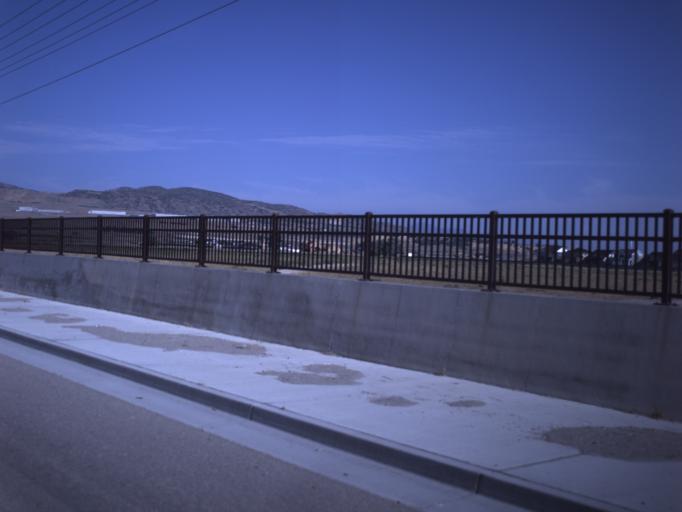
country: US
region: Utah
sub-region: Utah County
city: Lehi
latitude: 40.4132
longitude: -111.8953
